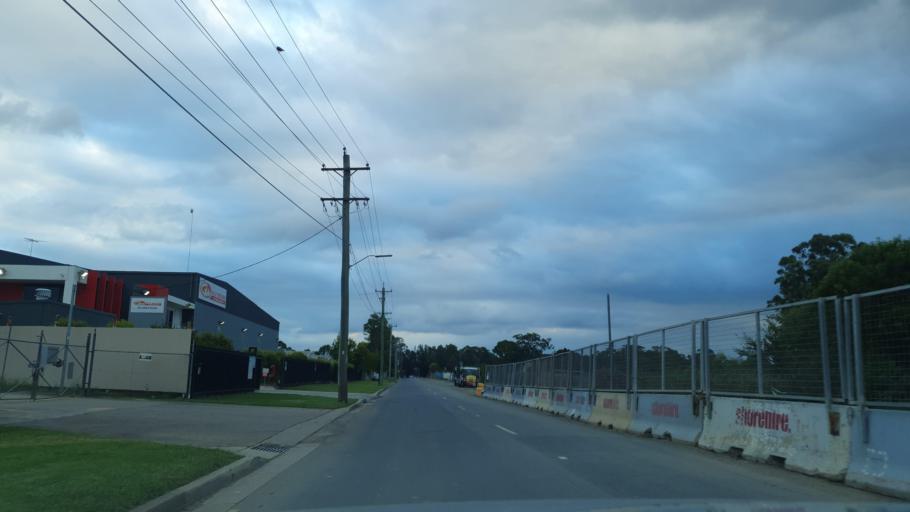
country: AU
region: New South Wales
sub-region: Penrith Municipality
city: Werrington County
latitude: -33.7382
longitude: 150.7648
